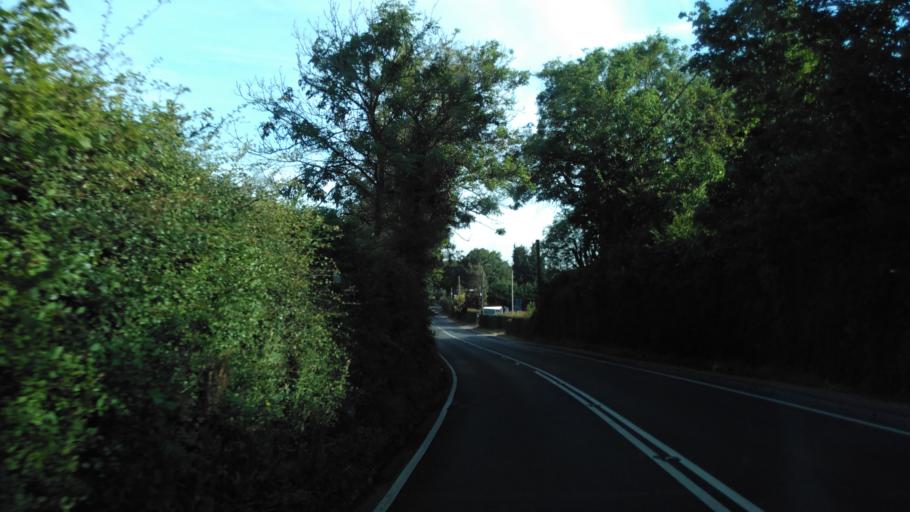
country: GB
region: England
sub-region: Kent
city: Blean
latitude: 51.3162
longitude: 1.0340
